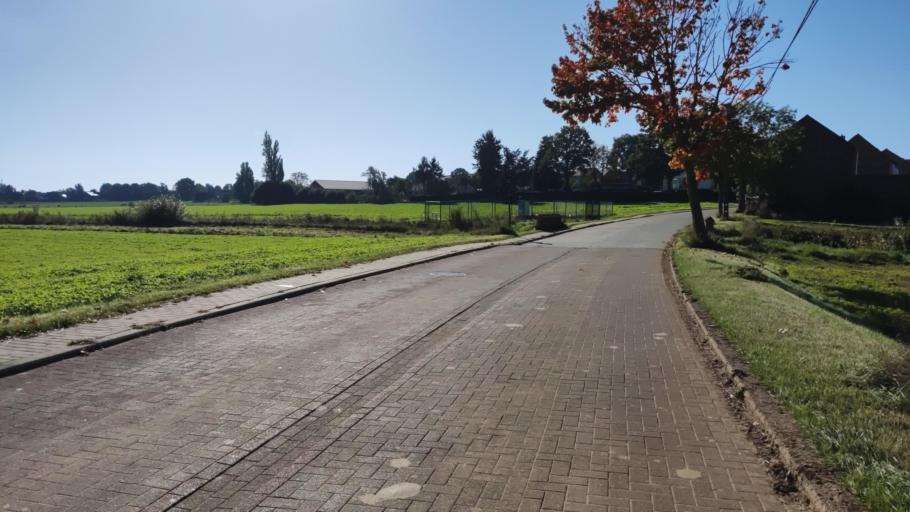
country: BE
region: Flanders
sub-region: Provincie Vlaams-Brabant
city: Tienen
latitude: 50.8180
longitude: 5.0055
